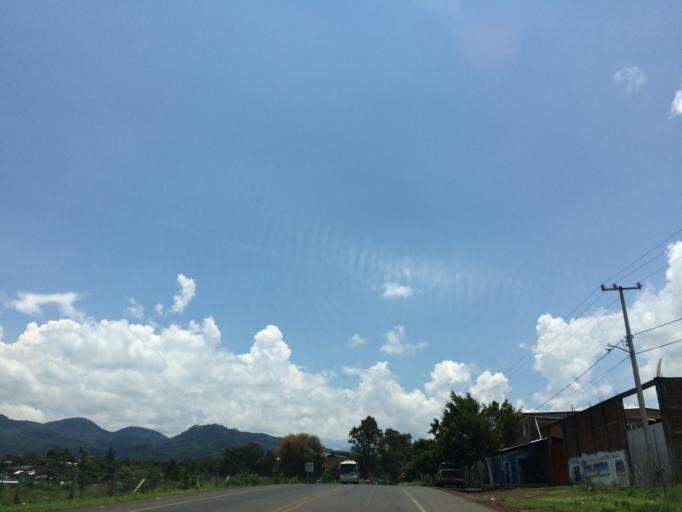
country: MX
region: Michoacan
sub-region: Periban
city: San Francisco Periban
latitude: 19.5495
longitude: -102.4029
